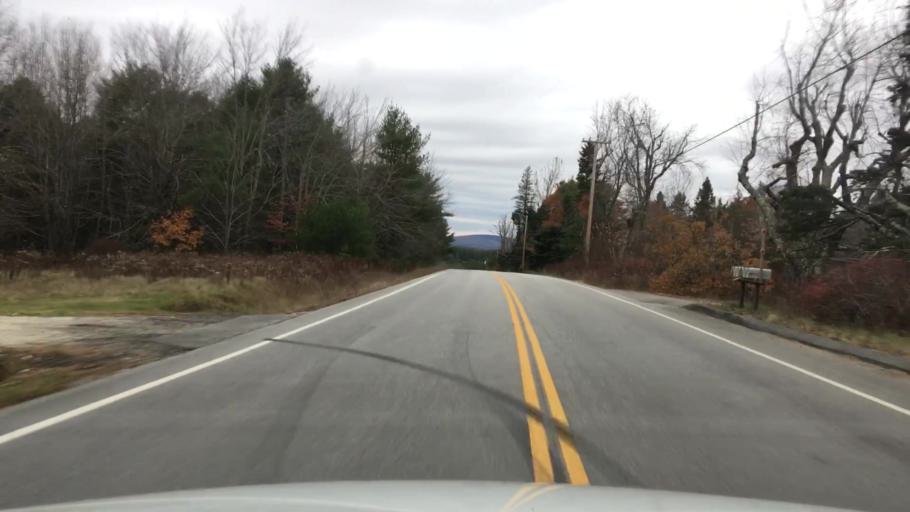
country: US
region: Maine
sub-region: Hancock County
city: Orland
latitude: 44.5344
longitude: -68.6776
